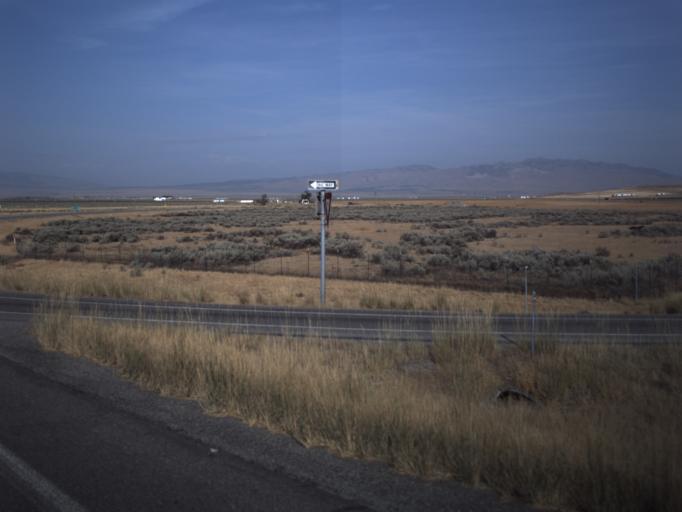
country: US
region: Idaho
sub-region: Oneida County
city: Malad City
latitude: 41.9637
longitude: -112.7598
